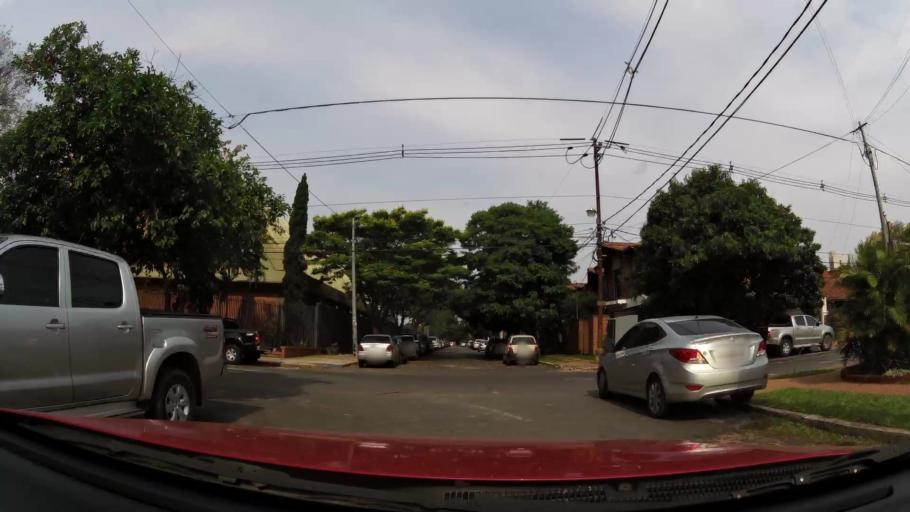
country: PY
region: Central
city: Fernando de la Mora
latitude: -25.2843
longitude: -57.5576
